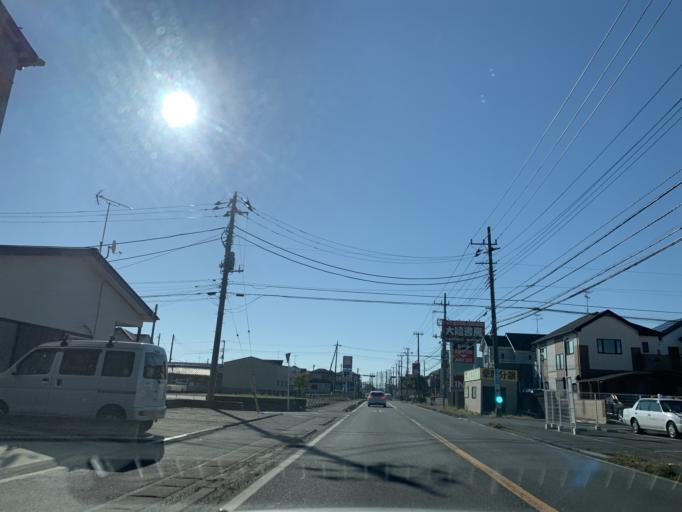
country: JP
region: Chiba
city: Matsudo
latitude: 35.8076
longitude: 139.8951
